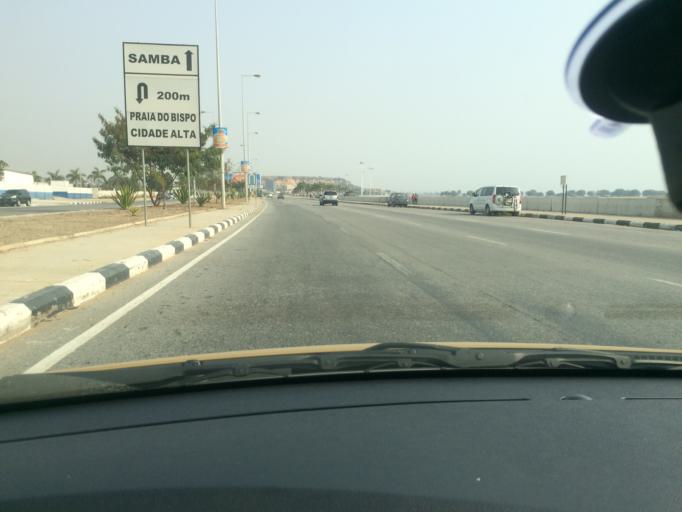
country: AO
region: Luanda
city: Luanda
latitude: -8.8196
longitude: 13.2165
